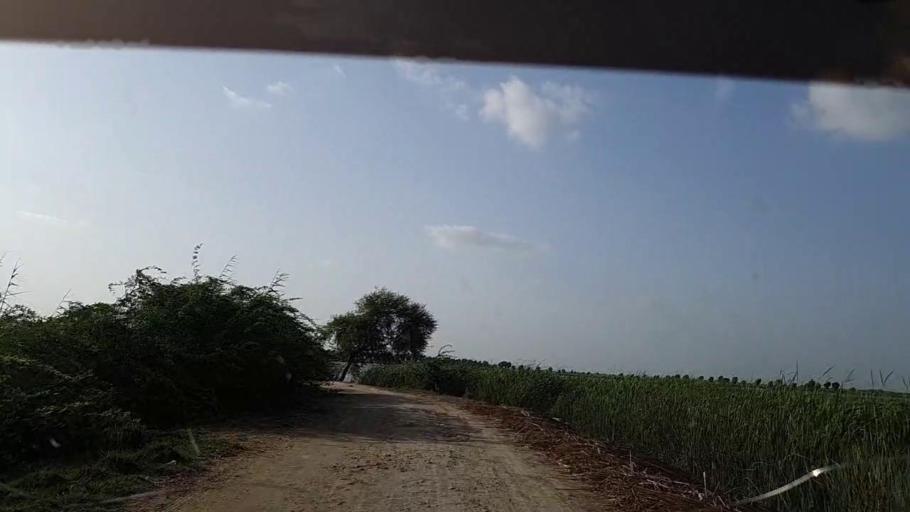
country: PK
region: Sindh
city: Badin
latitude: 24.5584
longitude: 68.8905
